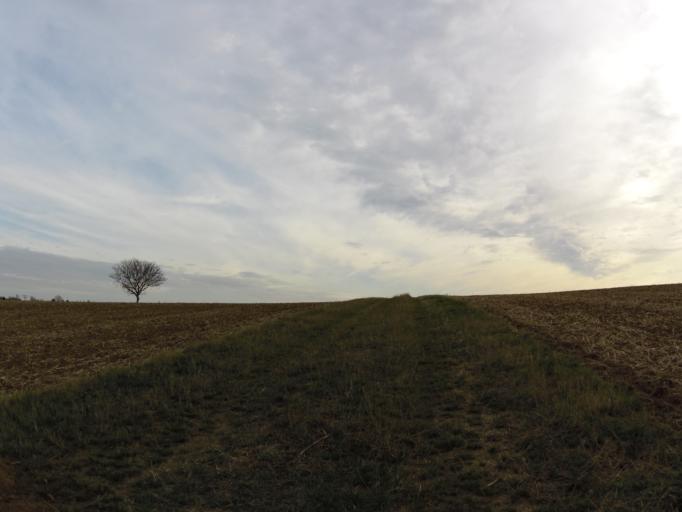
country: DE
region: Bavaria
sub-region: Regierungsbezirk Unterfranken
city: Eisingen
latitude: 49.7569
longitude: 9.8242
